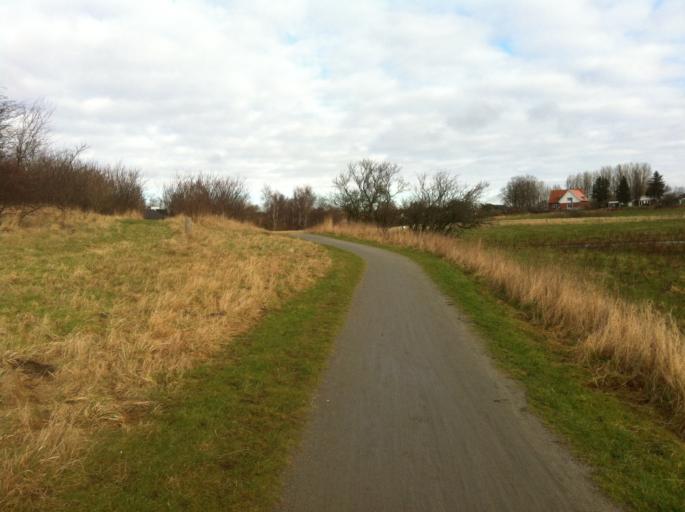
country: DK
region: South Denmark
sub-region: Odense Kommune
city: Odense
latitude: 55.4340
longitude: 10.3475
